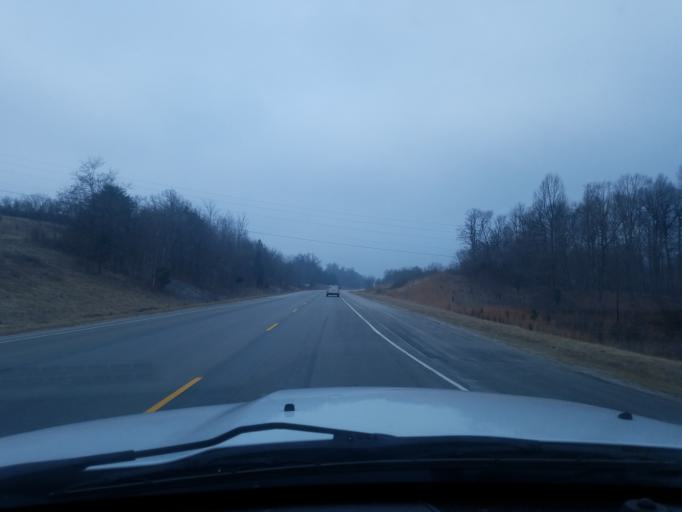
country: US
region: Indiana
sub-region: Perry County
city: Tell City
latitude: 38.0806
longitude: -86.6145
